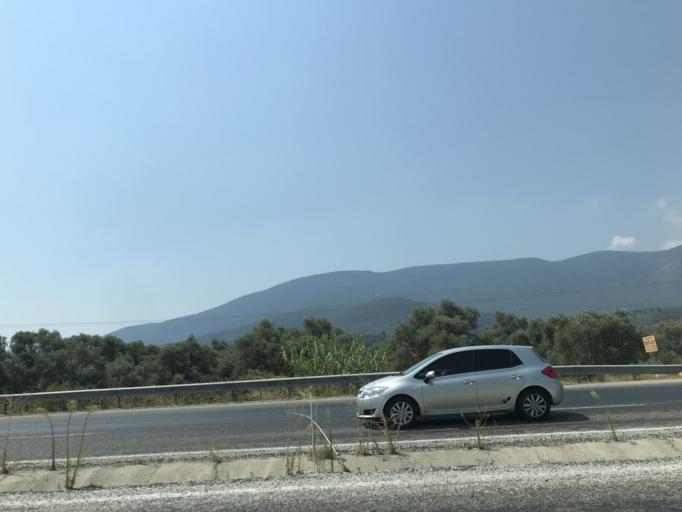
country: TR
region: Mugla
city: Selimiye
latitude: 37.4123
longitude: 27.6247
